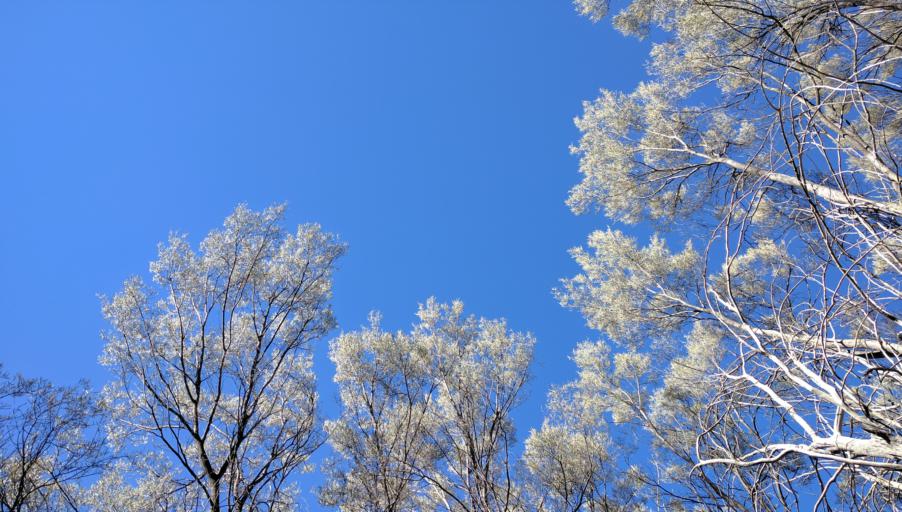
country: AU
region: Northern Territory
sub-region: Alice Springs
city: Alice Springs
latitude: -23.7388
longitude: 132.9389
